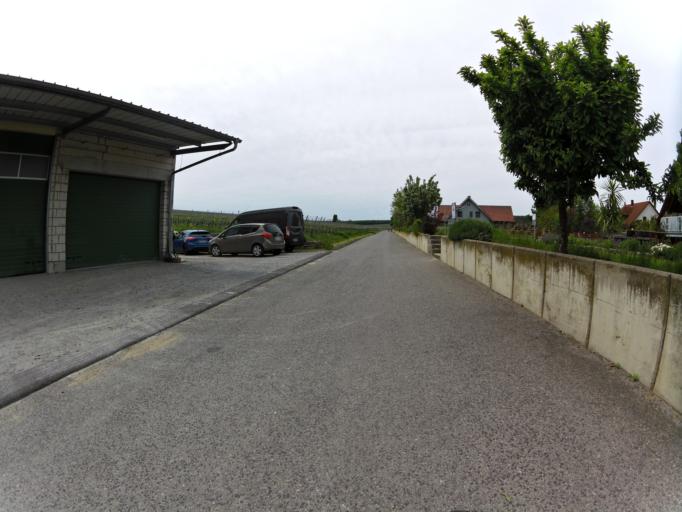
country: DE
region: Bavaria
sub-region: Regierungsbezirk Unterfranken
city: Nordheim
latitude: 49.8580
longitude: 10.1894
